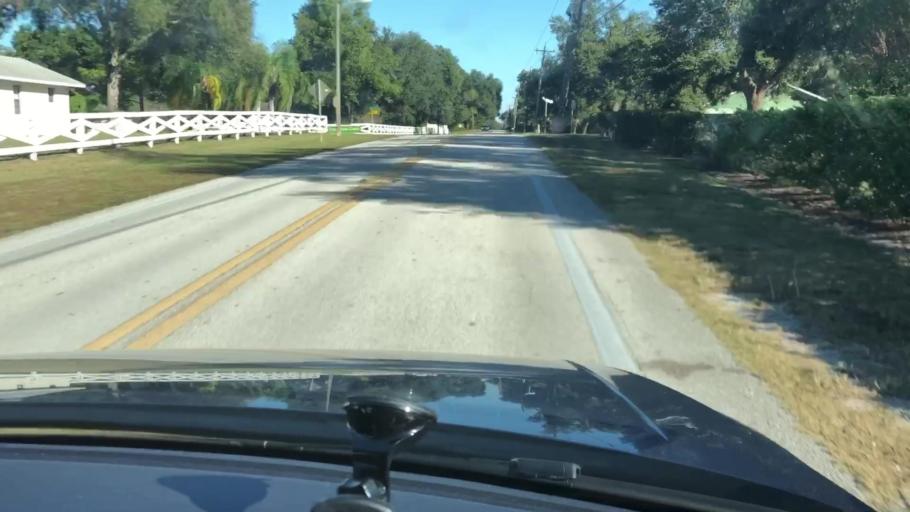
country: US
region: Florida
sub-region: Polk County
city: Gibsonia
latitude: 28.1322
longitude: -81.9383
